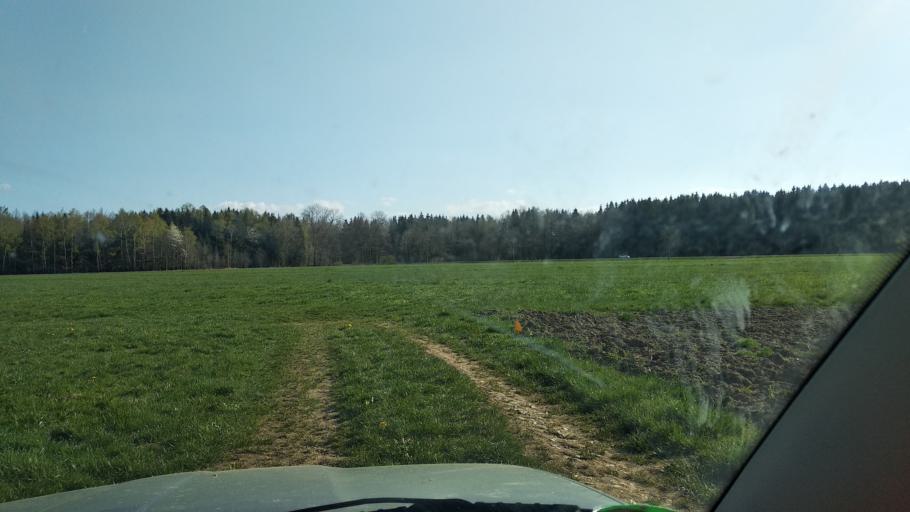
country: DE
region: Bavaria
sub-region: Swabia
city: Hawangen
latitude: 47.9598
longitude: 10.2587
